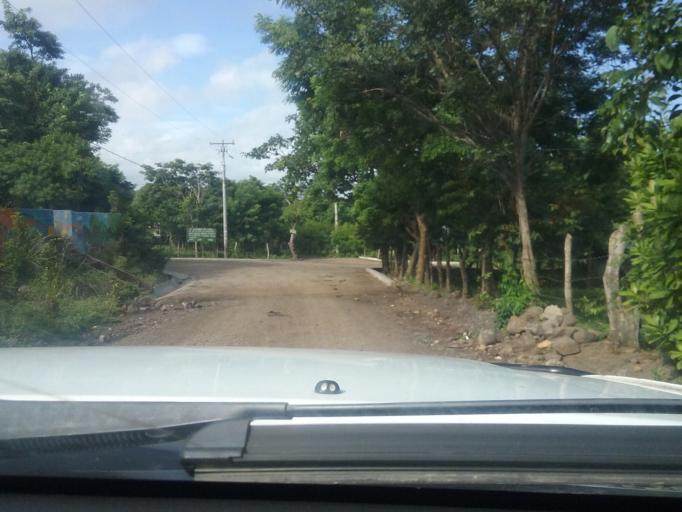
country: NI
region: Matagalpa
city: Matagalpa
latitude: 12.8827
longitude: -85.9659
